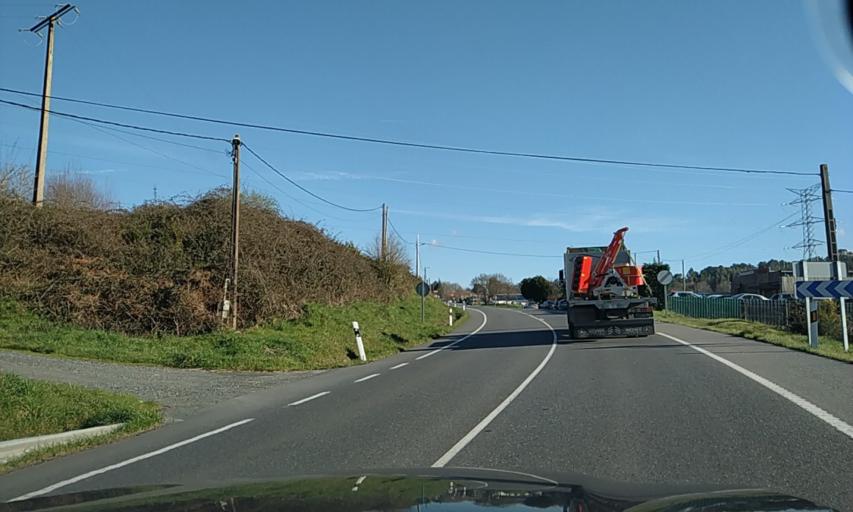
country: ES
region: Galicia
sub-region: Provincia de Pontevedra
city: Silleda
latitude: 42.7131
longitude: -8.2794
